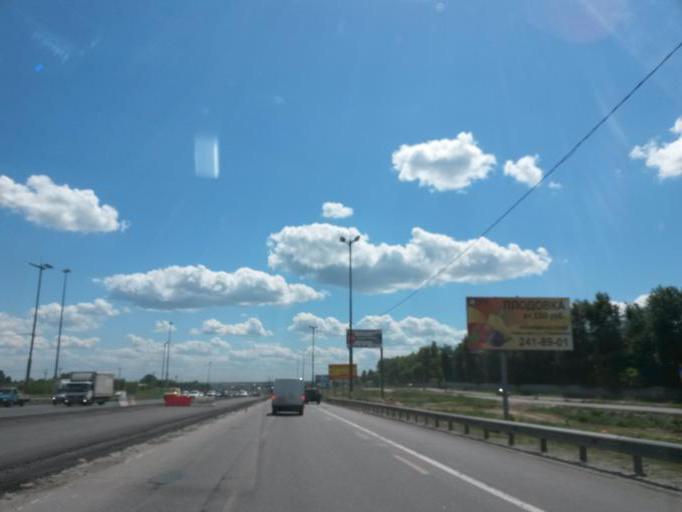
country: RU
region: Moskovskaya
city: Shcherbinka
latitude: 55.4796
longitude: 37.6146
